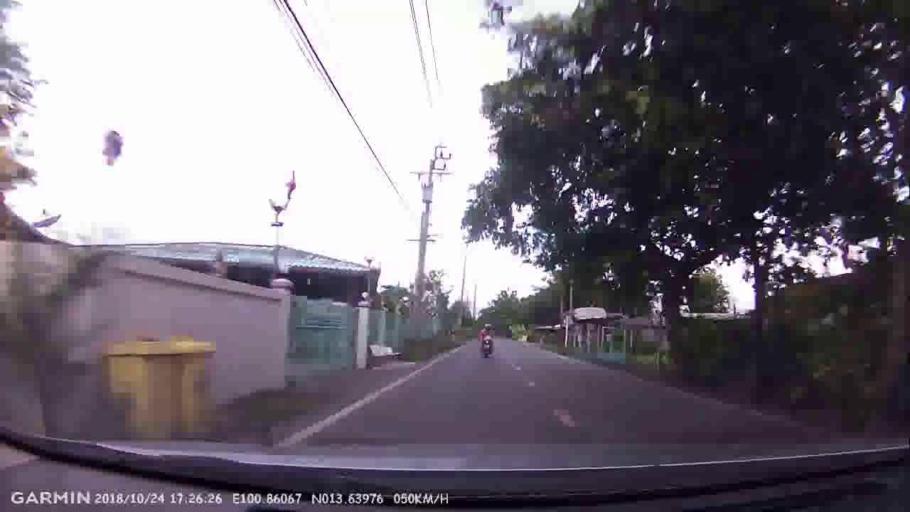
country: TH
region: Samut Prakan
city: Ban Khlong Bang Sao Thong
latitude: 13.6399
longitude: 100.8608
